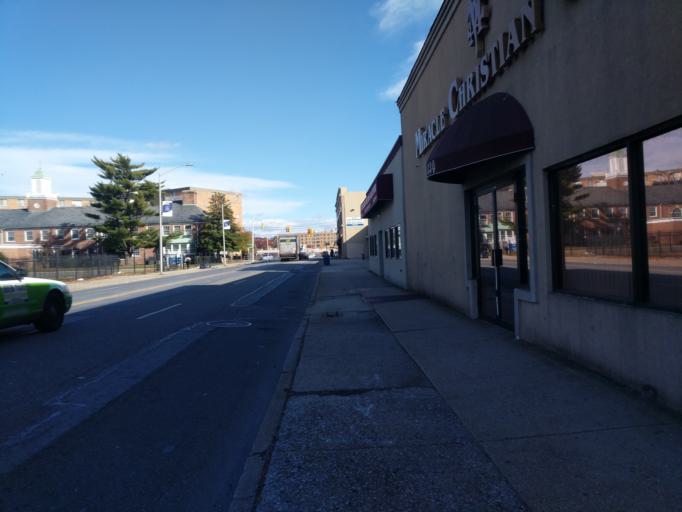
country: US
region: New York
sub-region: Nassau County
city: Hempstead
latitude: 40.7088
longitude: -73.6224
